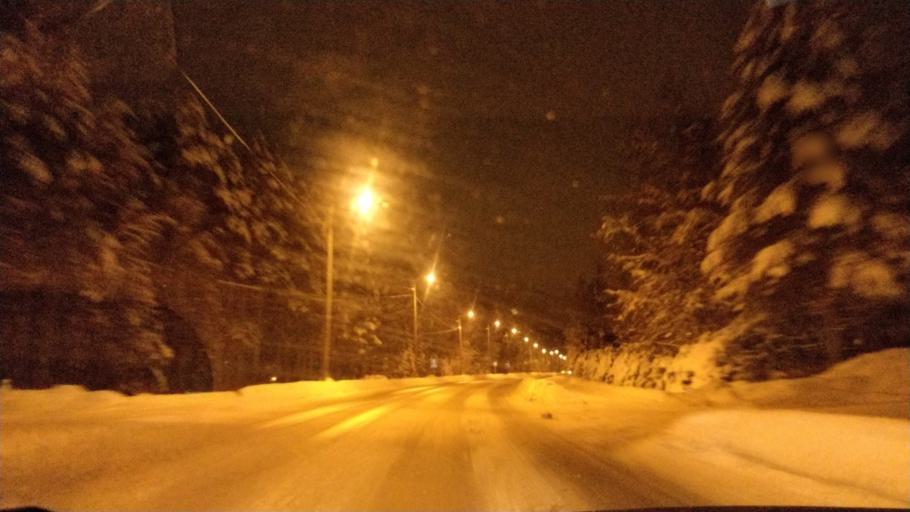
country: FI
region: Lapland
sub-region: Rovaniemi
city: Rovaniemi
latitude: 66.3741
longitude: 25.3829
